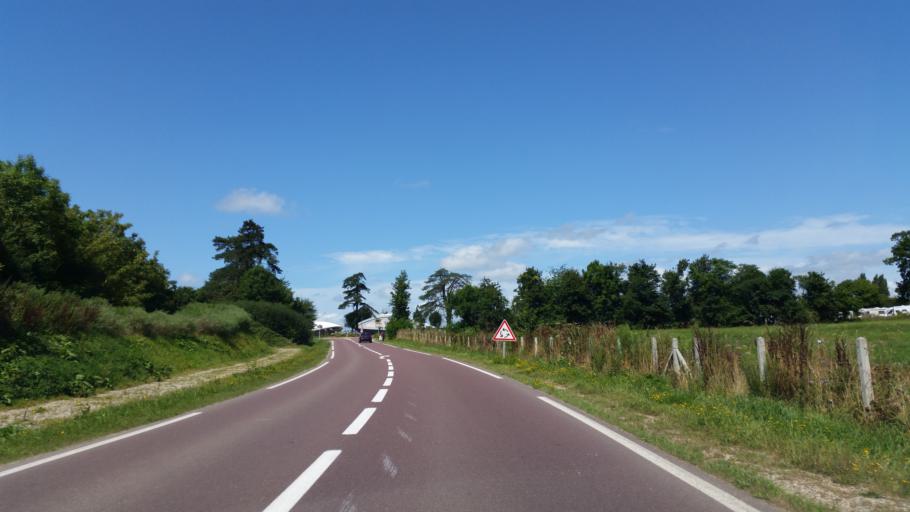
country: FR
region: Lower Normandy
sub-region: Departement de la Manche
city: Sainte-Mere-Eglise
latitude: 49.4060
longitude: -1.3110
